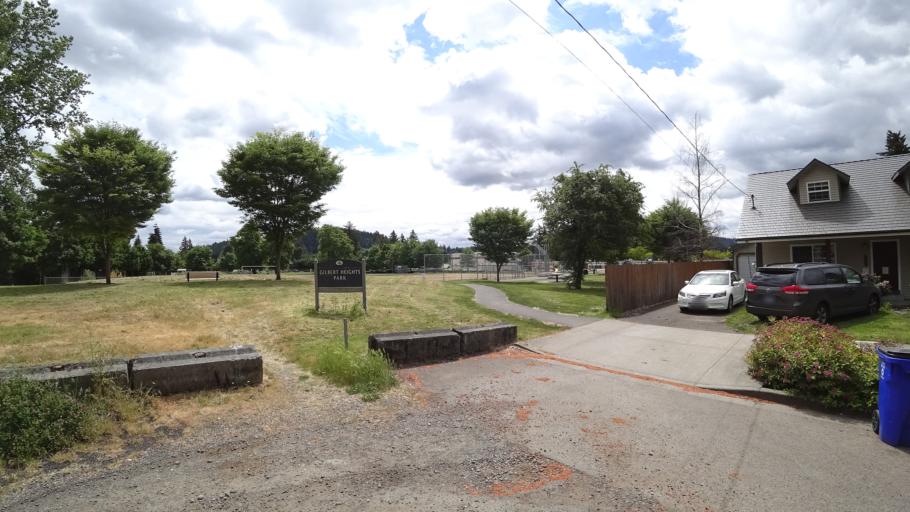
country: US
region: Oregon
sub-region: Multnomah County
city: Lents
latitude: 45.4921
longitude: -122.5326
